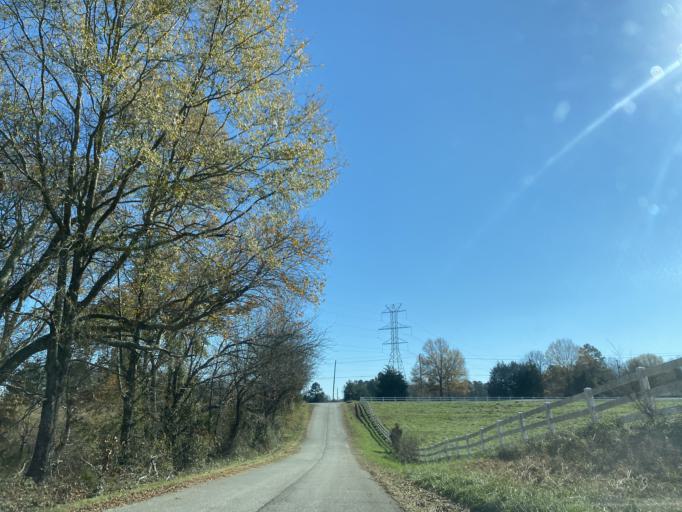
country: US
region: South Carolina
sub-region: Spartanburg County
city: Mayo
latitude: 35.1350
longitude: -81.7656
